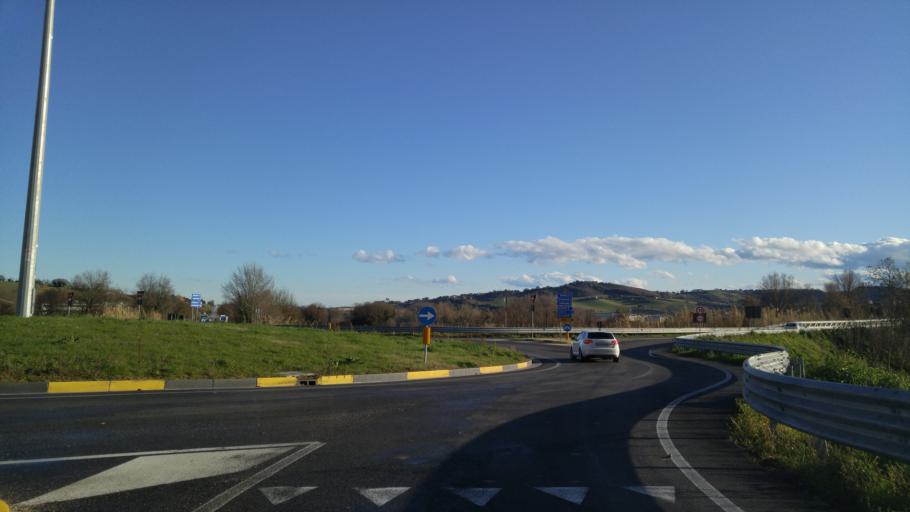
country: IT
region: The Marches
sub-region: Provincia di Ancona
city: Camerano
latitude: 43.5071
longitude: 13.5464
